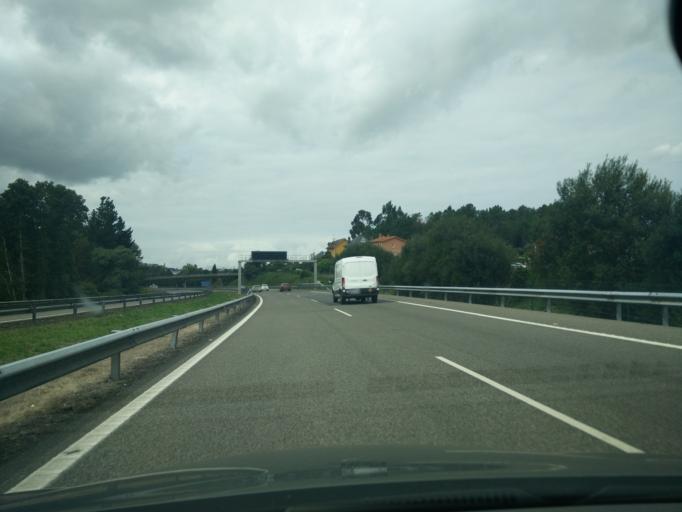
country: ES
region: Galicia
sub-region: Provincia da Coruna
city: Cambre
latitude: 43.3051
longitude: -8.3364
